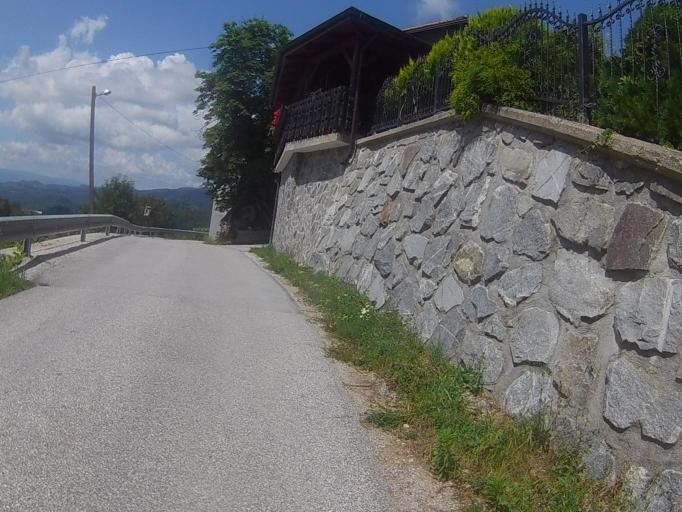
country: SI
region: Maribor
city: Kamnica
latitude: 46.6064
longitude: 15.6035
